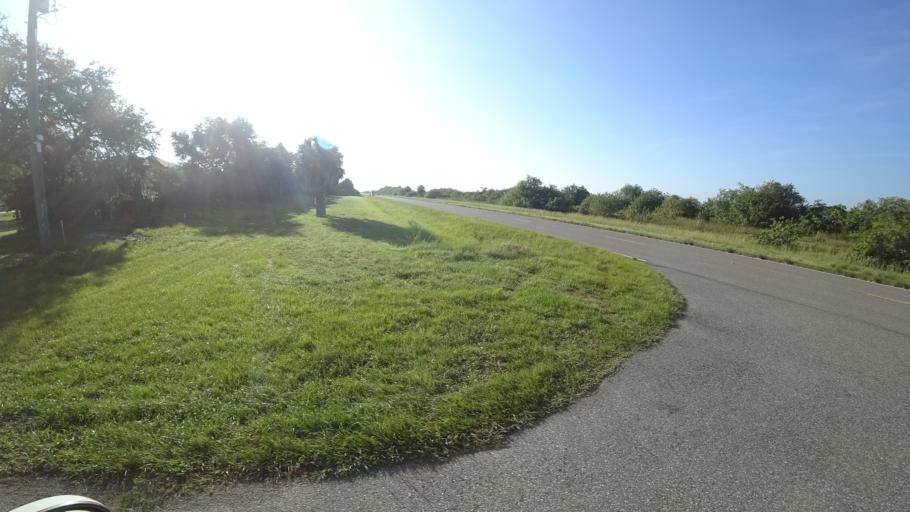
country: US
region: Florida
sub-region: Hillsborough County
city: Sun City Center
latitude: 27.5448
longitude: -82.3533
